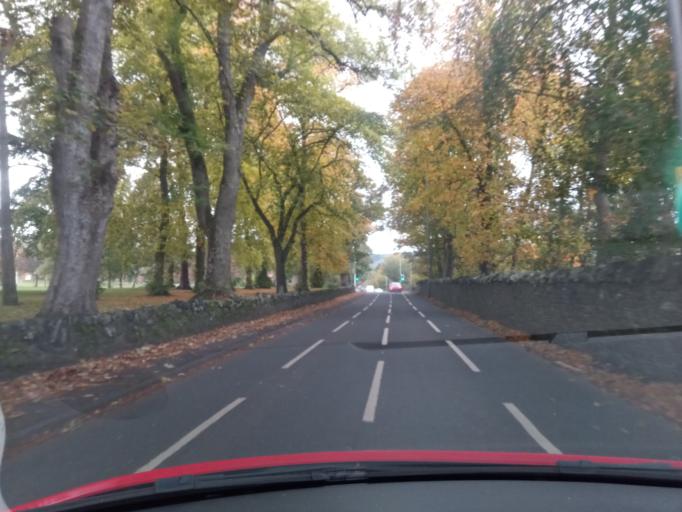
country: GB
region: Scotland
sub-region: The Scottish Borders
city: Peebles
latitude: 55.6490
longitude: -3.1860
